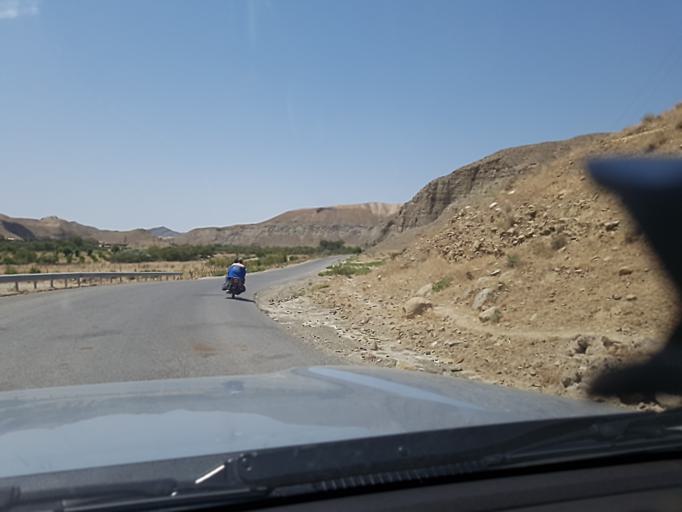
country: TM
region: Balkan
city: Magtymguly
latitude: 38.4483
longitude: 56.5227
